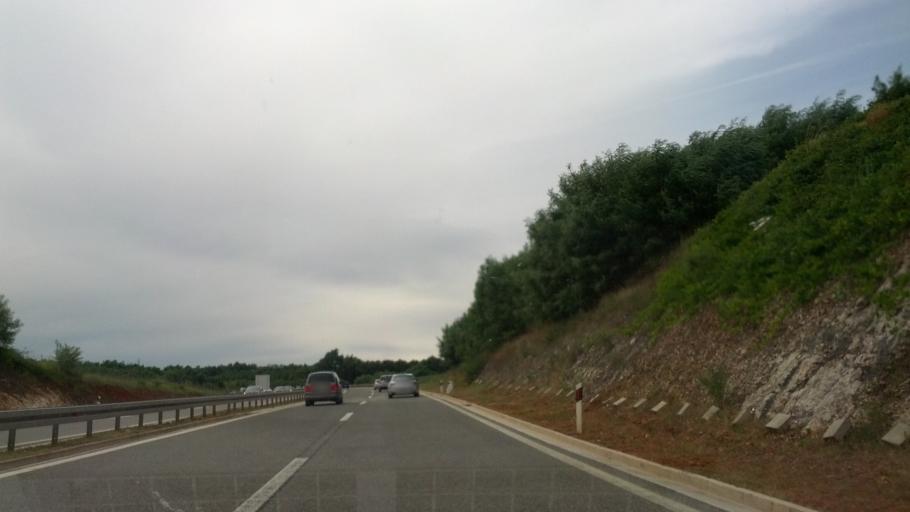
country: HR
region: Istarska
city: Buje
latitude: 45.3143
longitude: 13.7008
